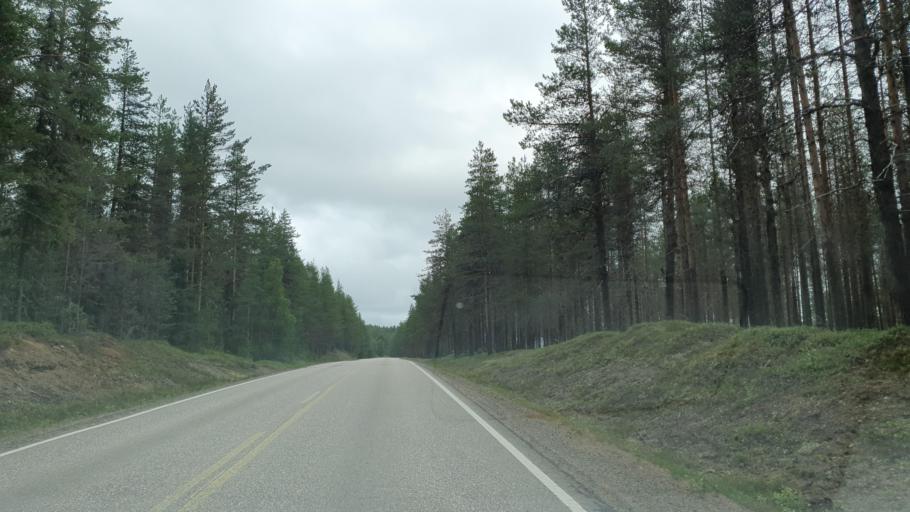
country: FI
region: Lapland
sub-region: Tunturi-Lappi
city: Kolari
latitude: 67.5702
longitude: 24.0505
